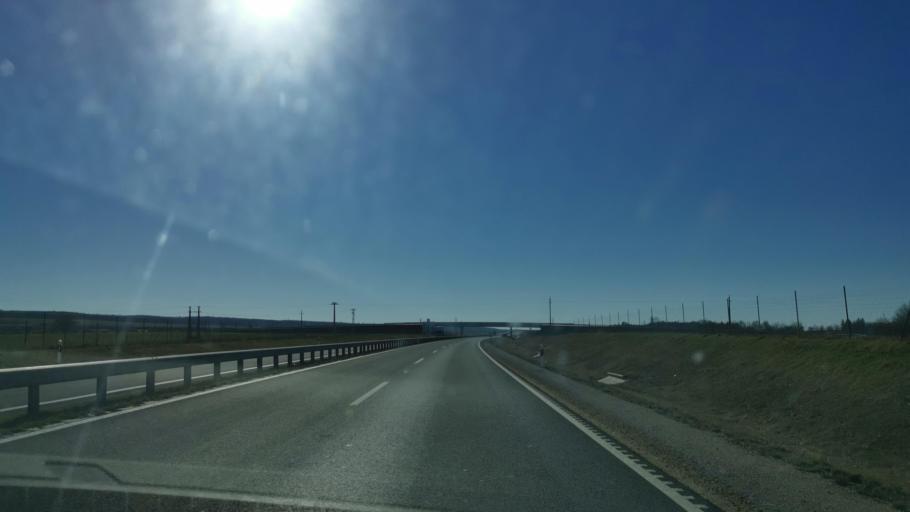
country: HU
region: Somogy
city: Balatonbereny
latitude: 46.6790
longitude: 17.2952
